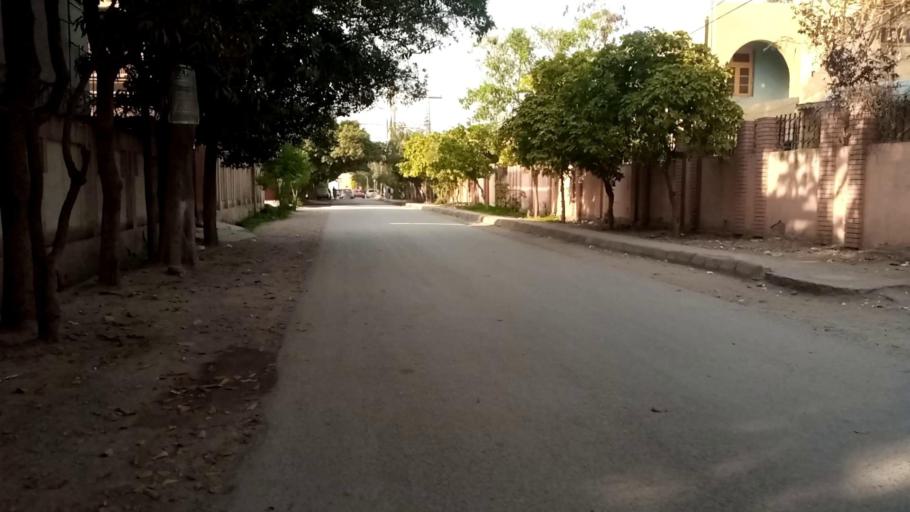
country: PK
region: Khyber Pakhtunkhwa
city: Peshawar
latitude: 33.9781
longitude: 71.4384
